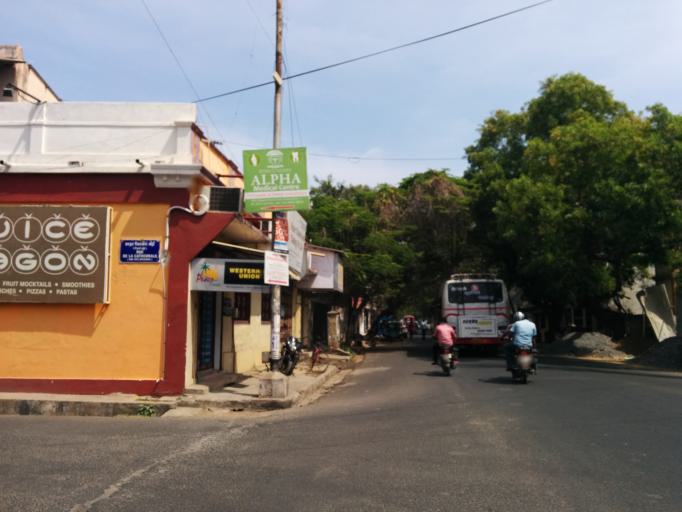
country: IN
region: Pondicherry
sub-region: Puducherry
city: Puducherry
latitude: 11.9292
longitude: 79.8299
